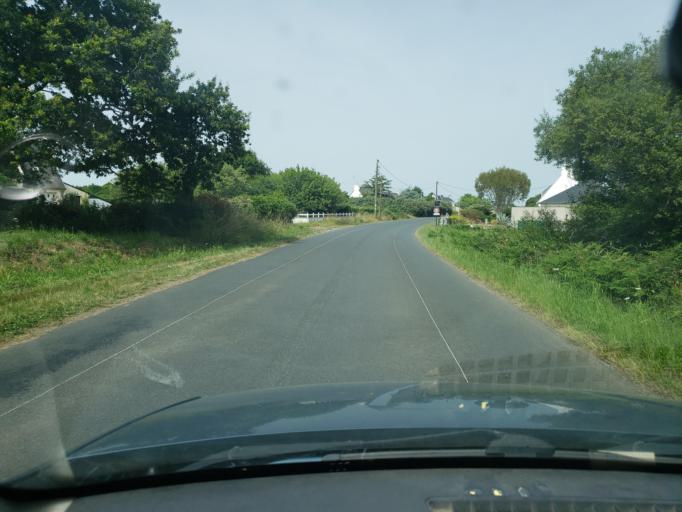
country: FR
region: Brittany
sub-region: Departement du Finistere
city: Plobannalec-Lesconil
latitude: 47.8153
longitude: -4.2381
